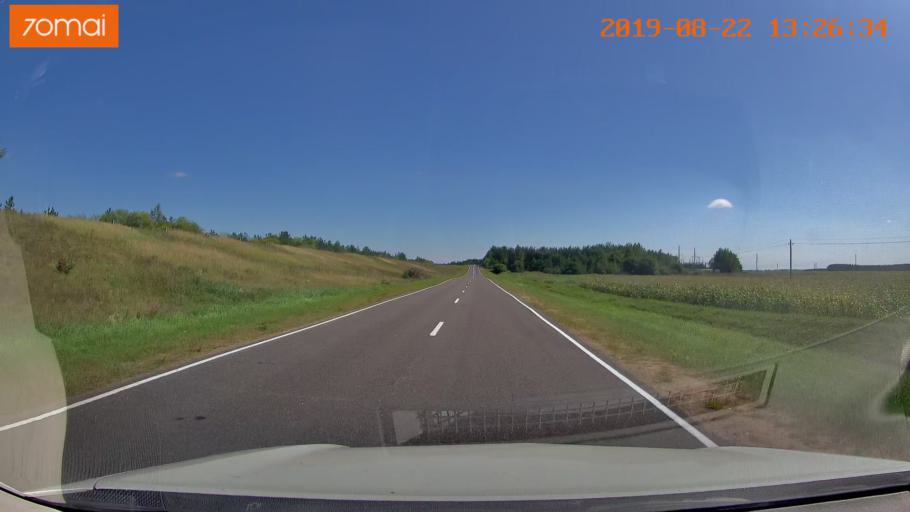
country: BY
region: Minsk
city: Staryya Darohi
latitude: 53.2090
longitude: 28.0651
